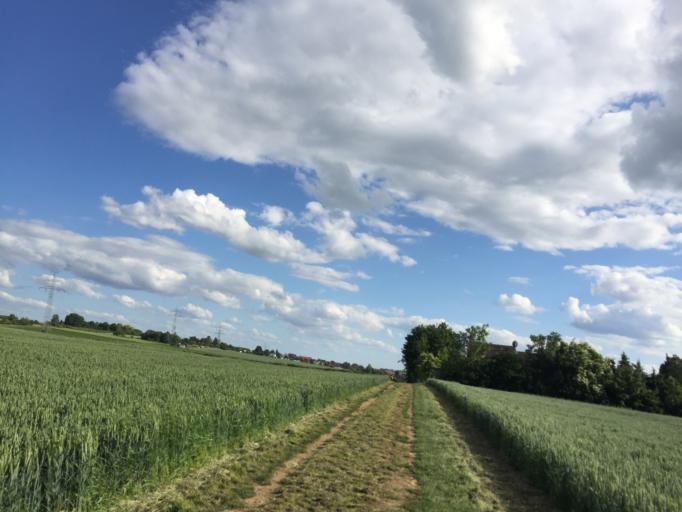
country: DE
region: Hesse
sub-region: Regierungsbezirk Darmstadt
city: Karben
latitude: 50.2327
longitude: 8.7795
